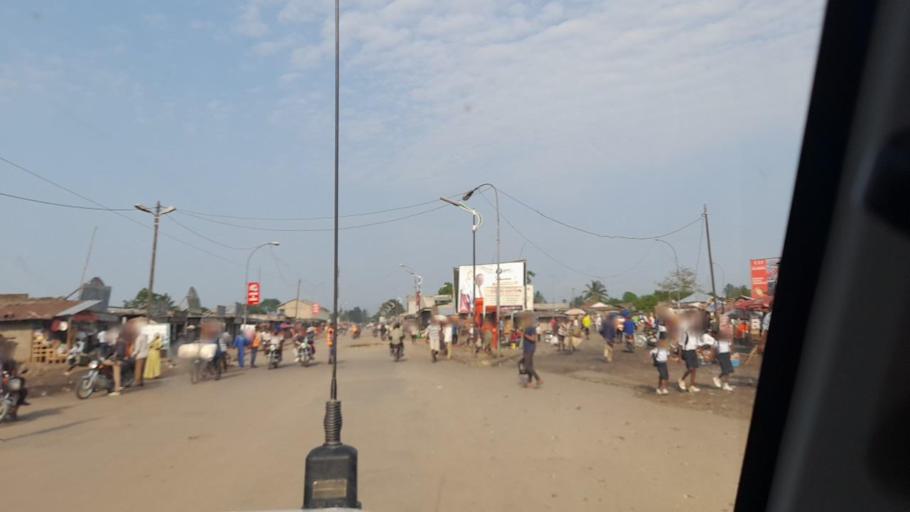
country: CD
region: Kasai-Occidental
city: Kananga
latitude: -5.8950
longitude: 22.3947
